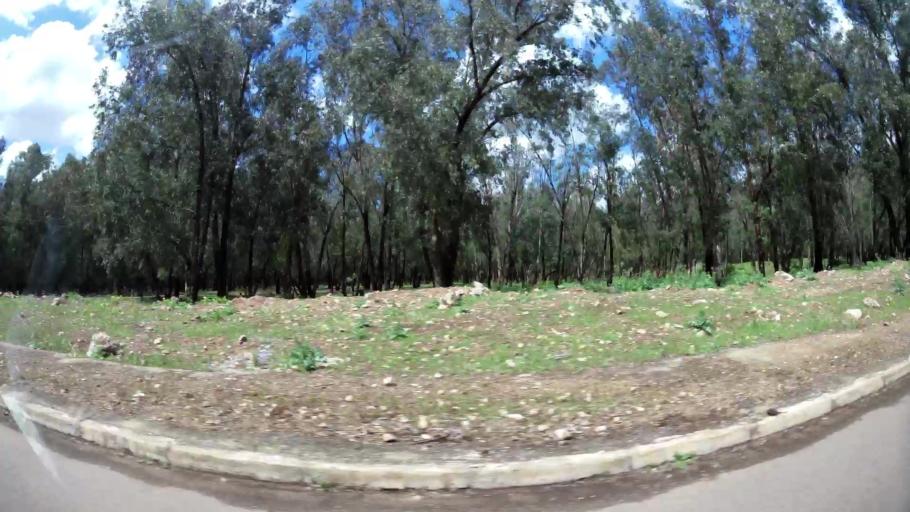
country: MA
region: Grand Casablanca
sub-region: Mediouna
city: Mediouna
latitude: 33.4000
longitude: -7.5581
